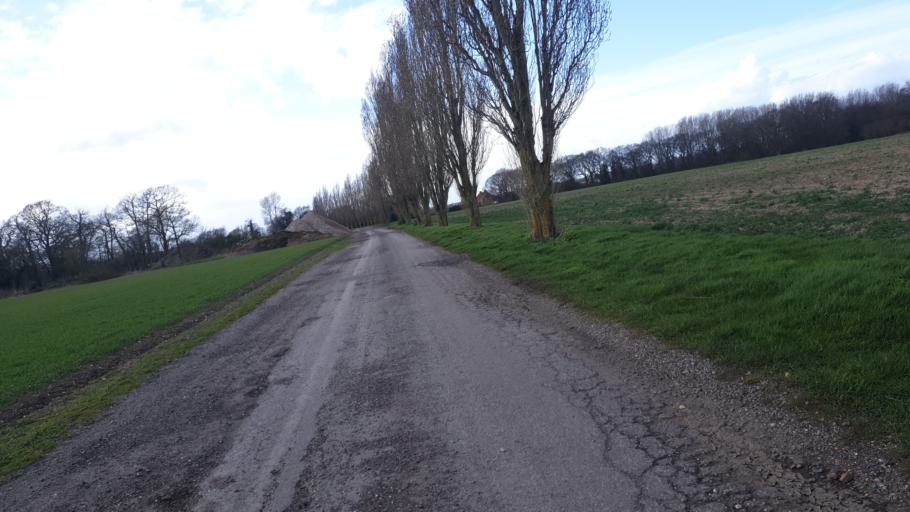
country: GB
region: England
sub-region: Essex
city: Little Clacton
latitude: 51.8506
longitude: 1.1327
